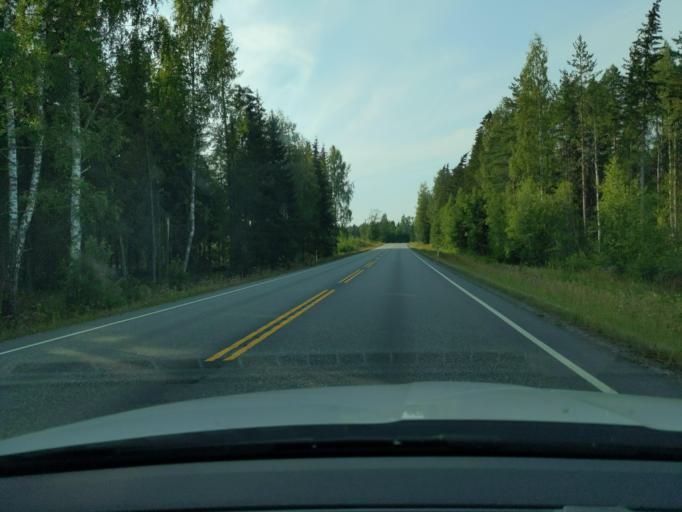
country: FI
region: Paijanne Tavastia
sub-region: Lahti
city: Padasjoki
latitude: 61.3189
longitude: 25.2847
